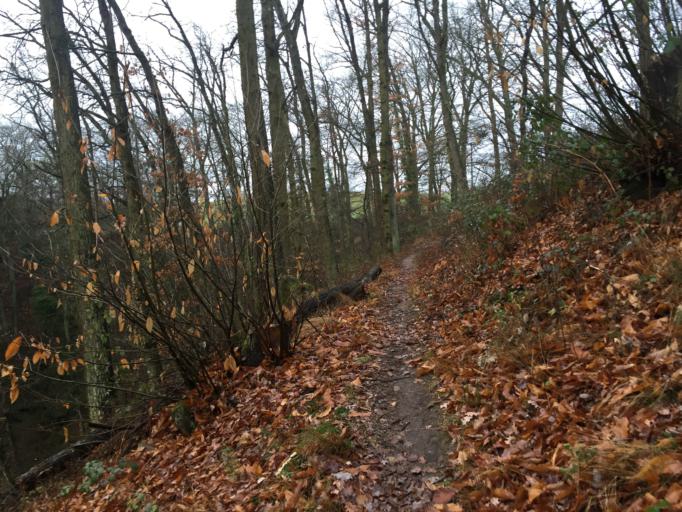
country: DE
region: Rheinland-Pfalz
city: Tiefenthal
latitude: 49.5318
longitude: 8.1084
